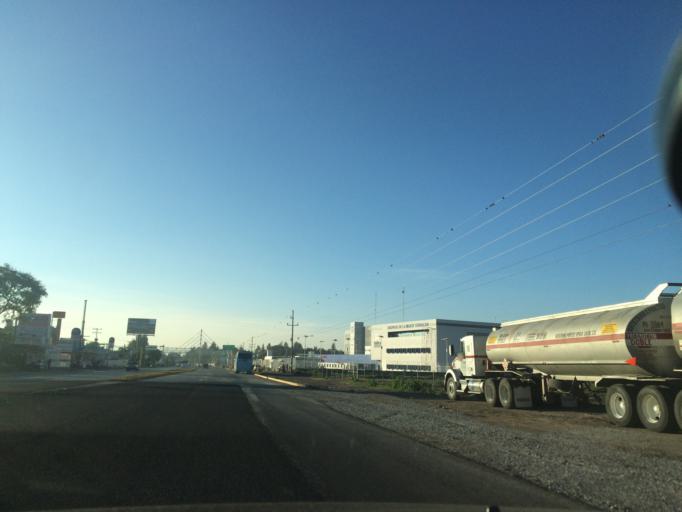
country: MX
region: Puebla
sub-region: Santiago Miahuatlan
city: San Jose Monte Chiquito
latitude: 18.4782
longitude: -97.4408
